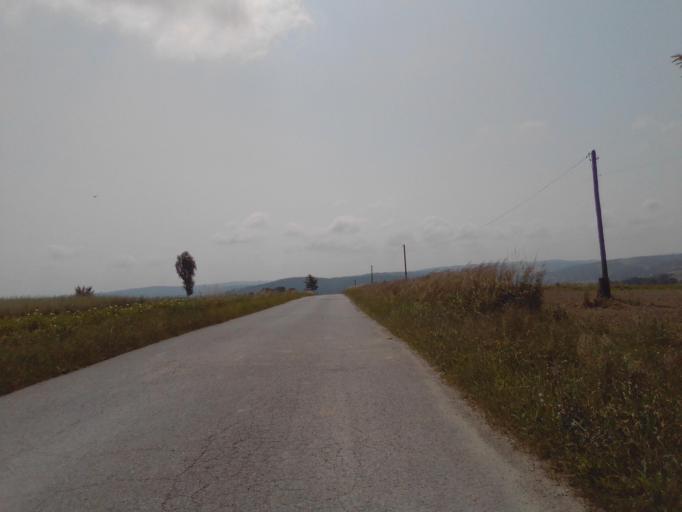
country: PL
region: Subcarpathian Voivodeship
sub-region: Powiat strzyzowski
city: Czudec
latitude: 49.9543
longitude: 21.8021
